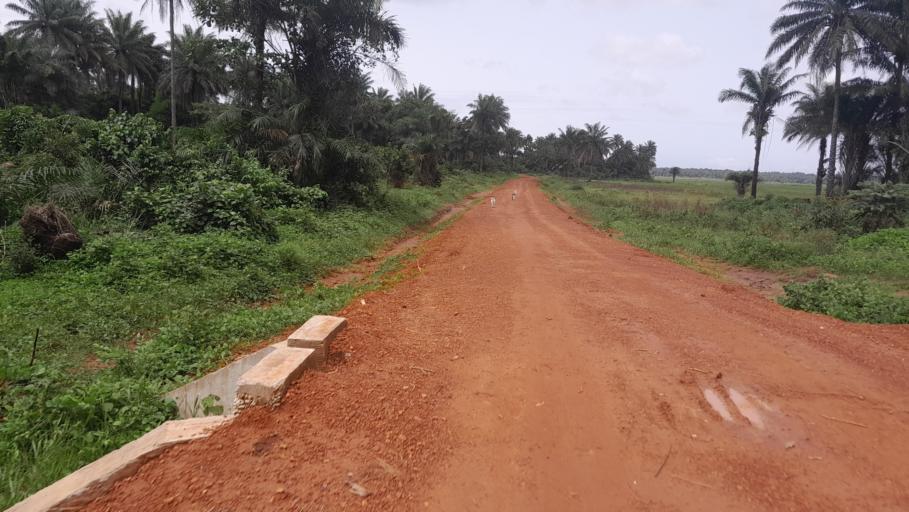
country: GN
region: Boke
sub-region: Boffa
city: Boffa
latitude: 9.9979
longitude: -13.8876
